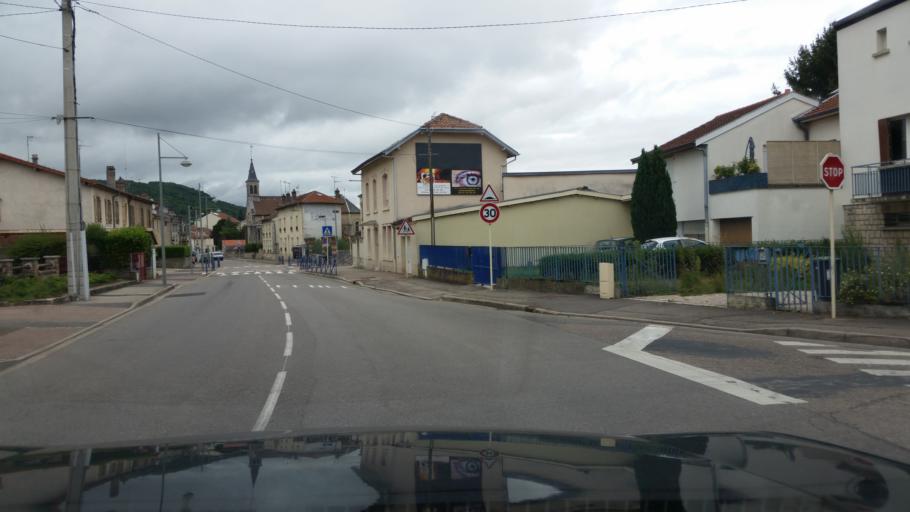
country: FR
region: Lorraine
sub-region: Departement de Meurthe-et-Moselle
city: Toul
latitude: 48.6683
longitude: 5.8823
